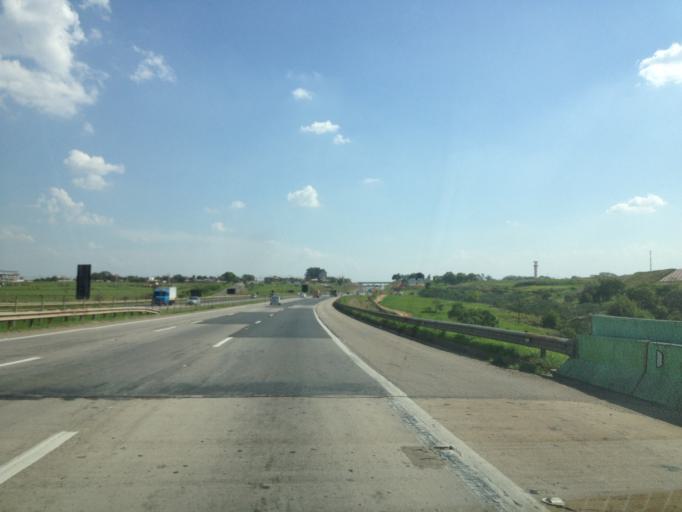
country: BR
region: Sao Paulo
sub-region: Indaiatuba
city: Indaiatuba
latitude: -23.0149
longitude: -47.1182
